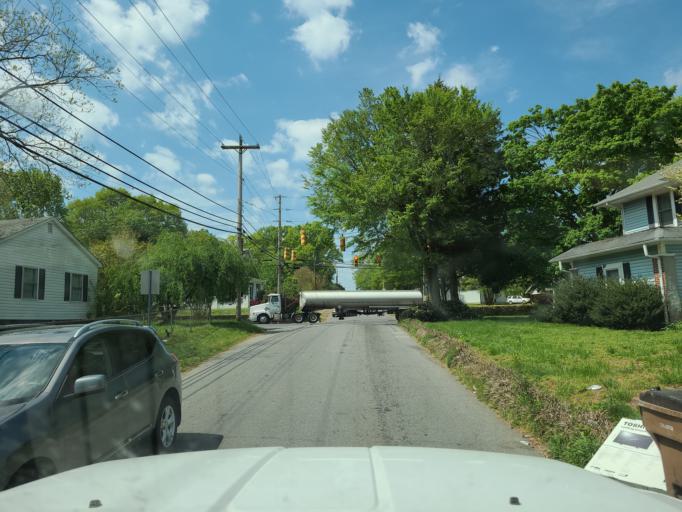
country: US
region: North Carolina
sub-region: Lincoln County
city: Lincolnton
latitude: 35.4727
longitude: -81.2625
